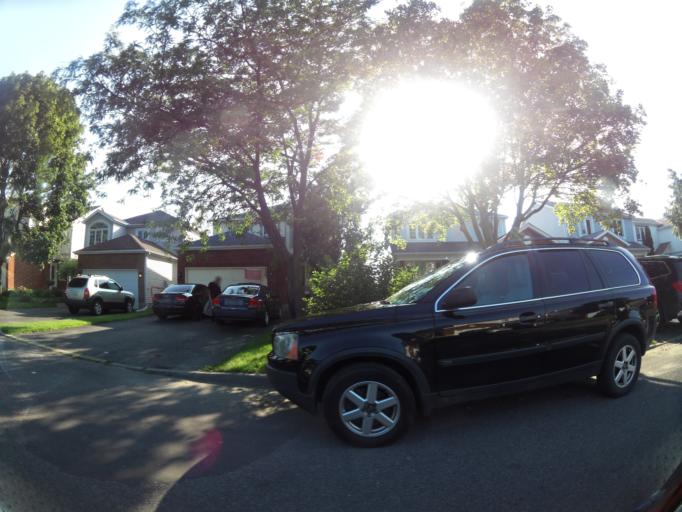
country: CA
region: Ontario
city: Clarence-Rockland
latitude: 45.4795
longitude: -75.4787
